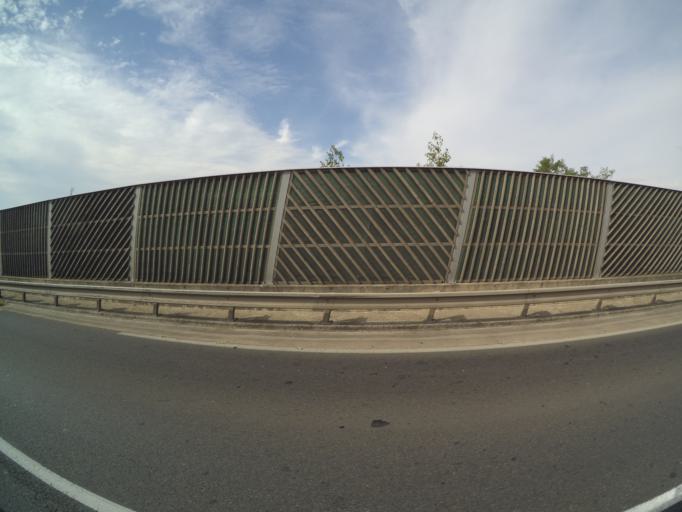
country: FR
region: Pays de la Loire
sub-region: Departement de Maine-et-Loire
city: Saumur
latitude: 47.2610
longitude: -0.0967
